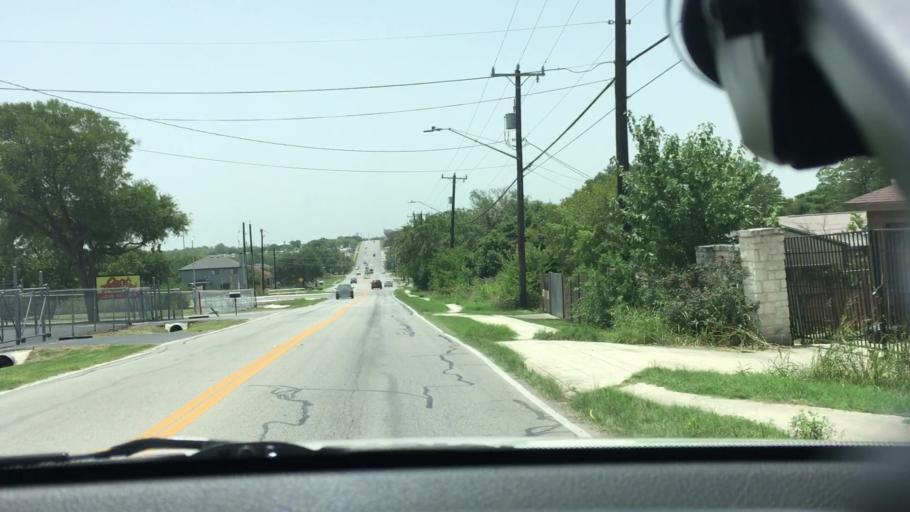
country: US
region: Texas
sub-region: Bexar County
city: Live Oak
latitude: 29.5731
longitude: -98.3586
